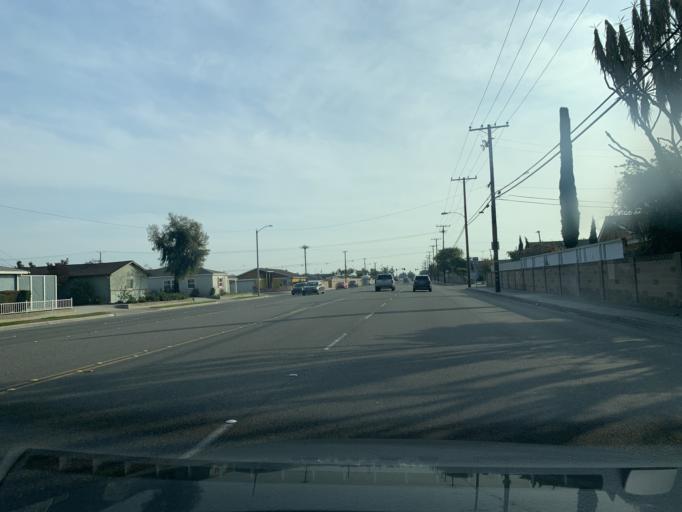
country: US
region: California
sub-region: Orange County
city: Westminster
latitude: 33.7550
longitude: -118.0247
